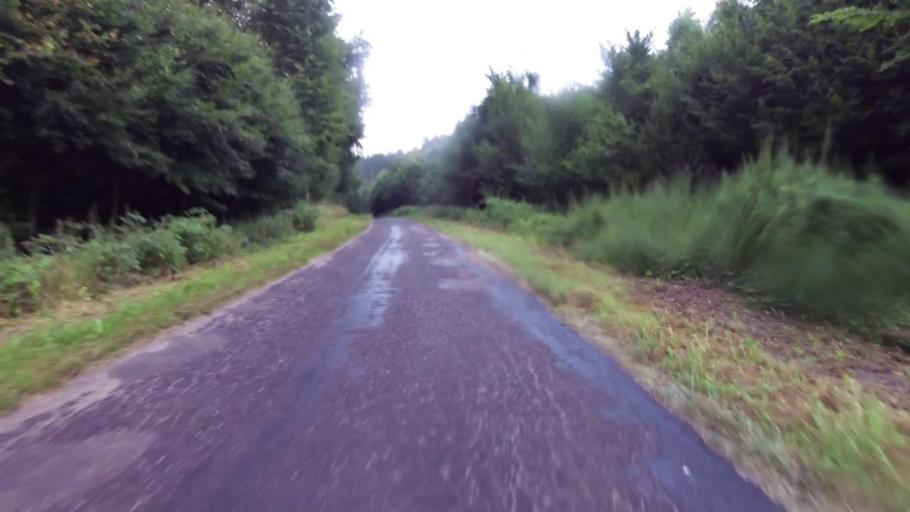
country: PL
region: West Pomeranian Voivodeship
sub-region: Powiat lobeski
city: Wegorzyno
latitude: 53.5217
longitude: 15.6466
